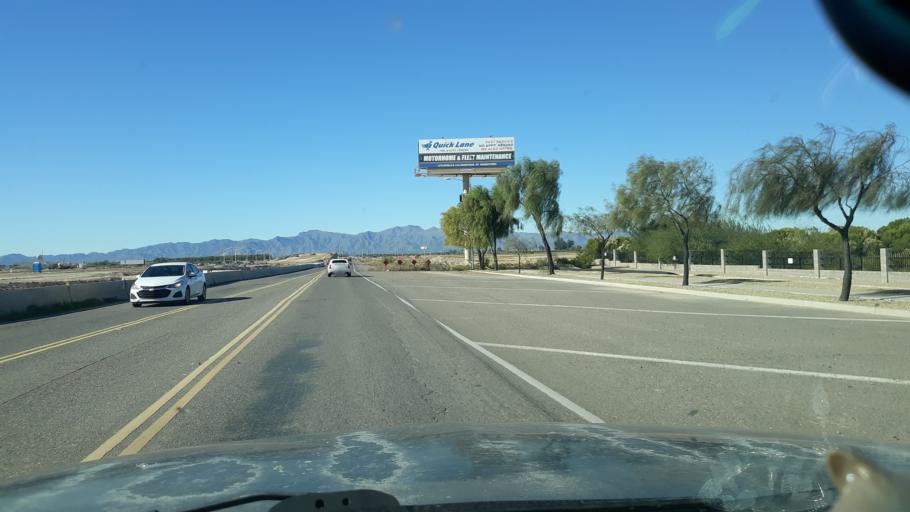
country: US
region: Arizona
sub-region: Maricopa County
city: Youngtown
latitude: 33.5512
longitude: -112.3322
